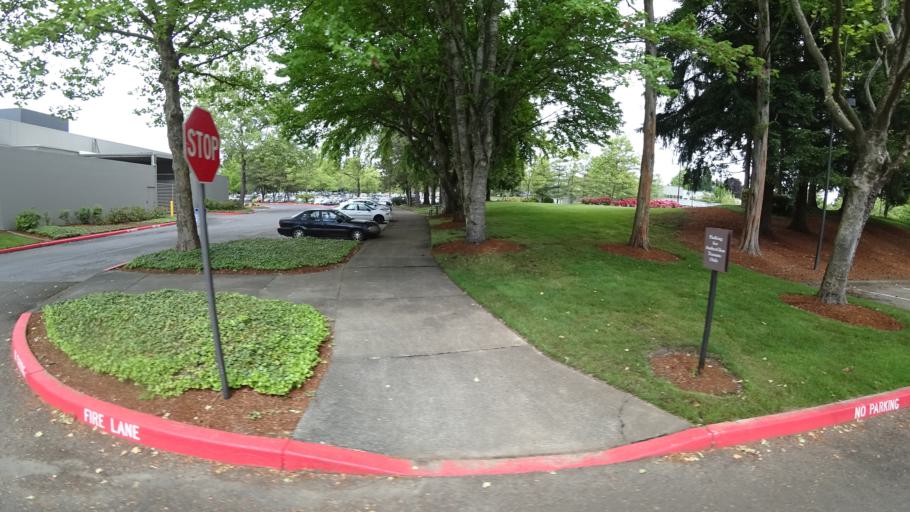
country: US
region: Oregon
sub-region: Washington County
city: Rockcreek
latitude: 45.5306
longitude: -122.8805
